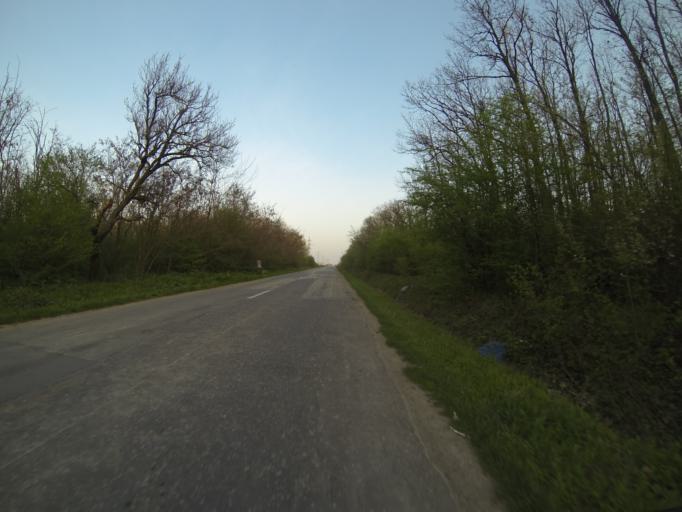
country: RO
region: Dolj
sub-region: Comuna Dranicu
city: Dranic
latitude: 44.0641
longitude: 23.8142
